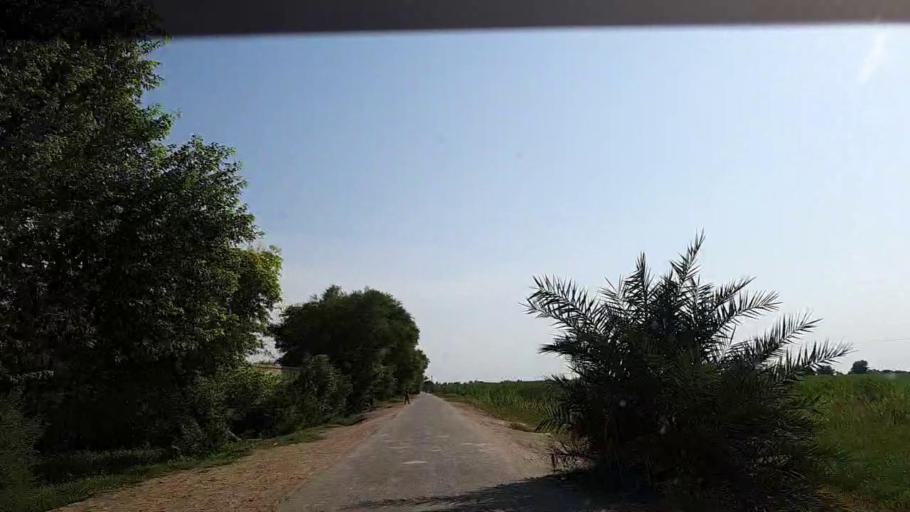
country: PK
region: Sindh
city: Adilpur
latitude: 27.9298
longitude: 69.2535
